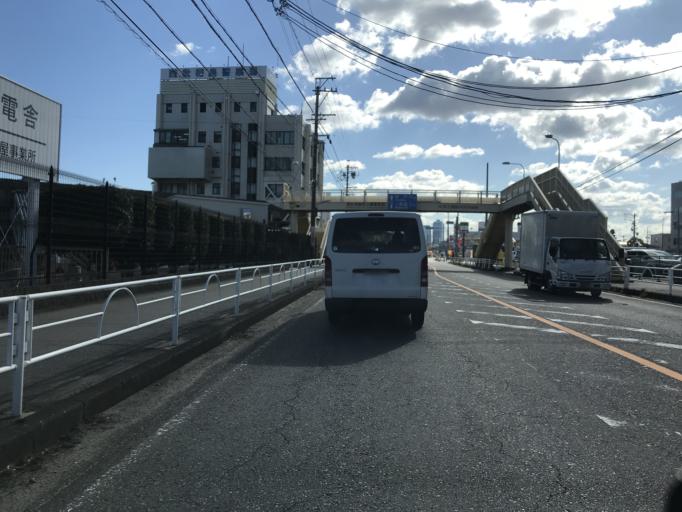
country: JP
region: Aichi
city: Nagoya-shi
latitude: 35.2018
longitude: 136.8619
